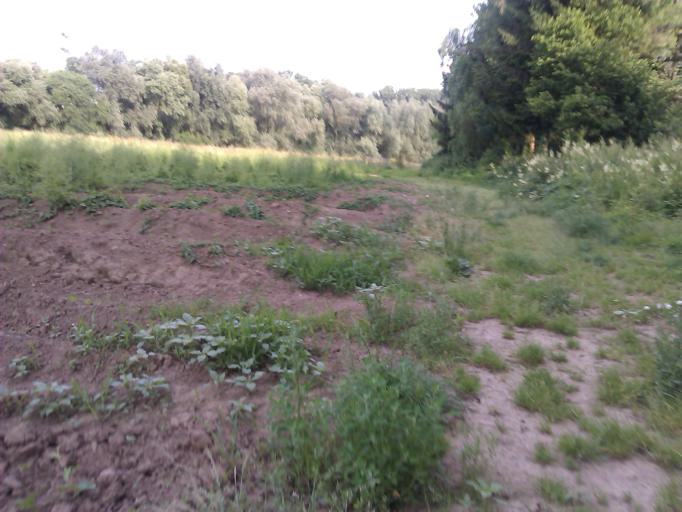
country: DE
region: Baden-Wuerttemberg
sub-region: Regierungsbezirk Stuttgart
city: Untereisesheim
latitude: 49.2058
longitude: 9.2112
